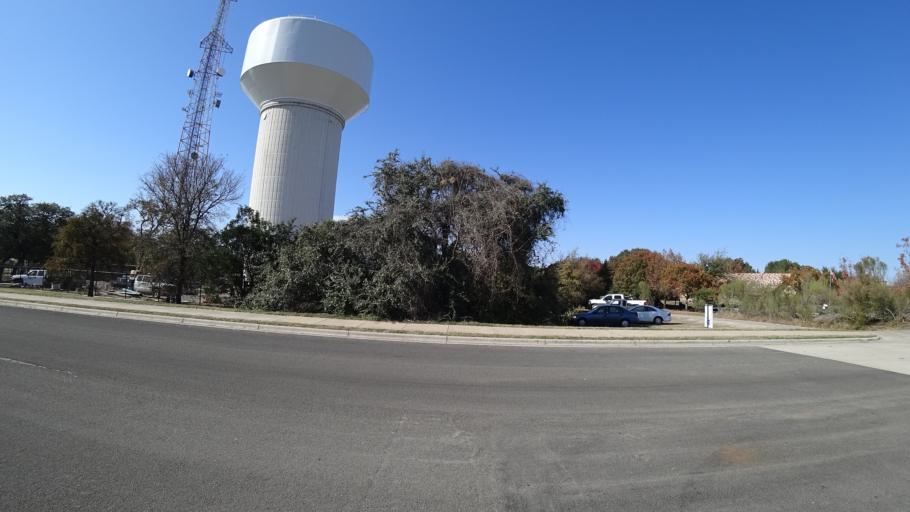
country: US
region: Texas
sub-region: Williamson County
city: Anderson Mill
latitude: 30.3906
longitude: -97.8428
